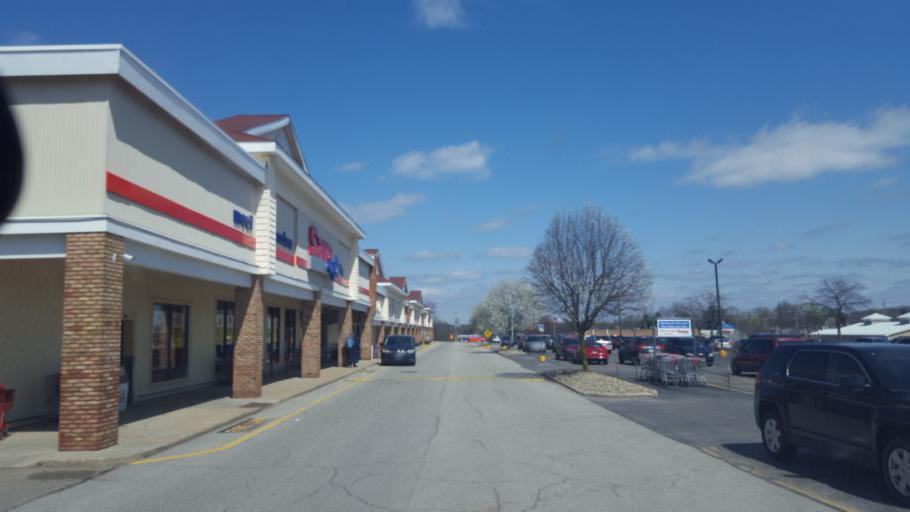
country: US
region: Ohio
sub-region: Geauga County
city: Middlefield
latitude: 41.4604
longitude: -81.0867
